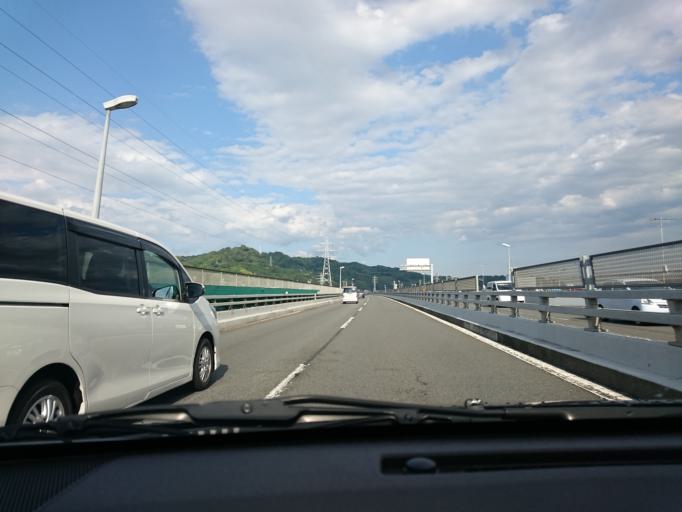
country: JP
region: Kanagawa
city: Odawara
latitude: 35.2903
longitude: 139.1868
